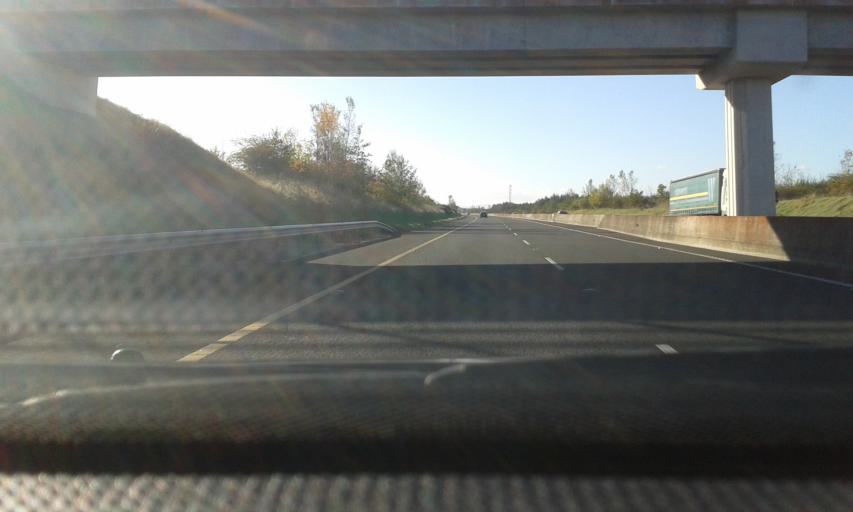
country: IE
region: Munster
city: Thurles
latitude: 52.6841
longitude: -7.6757
